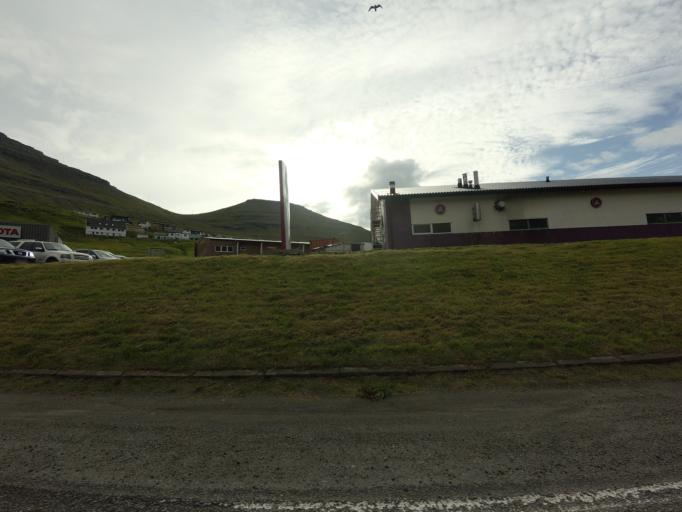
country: FO
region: Nordoyar
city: Klaksvik
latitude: 62.2211
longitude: -6.5745
